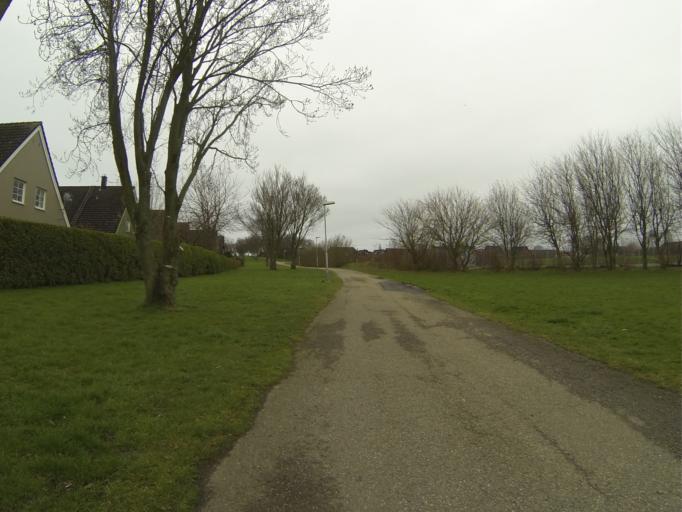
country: SE
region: Skane
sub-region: Simrishamns Kommun
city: Simrishamn
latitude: 55.5444
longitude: 14.3465
